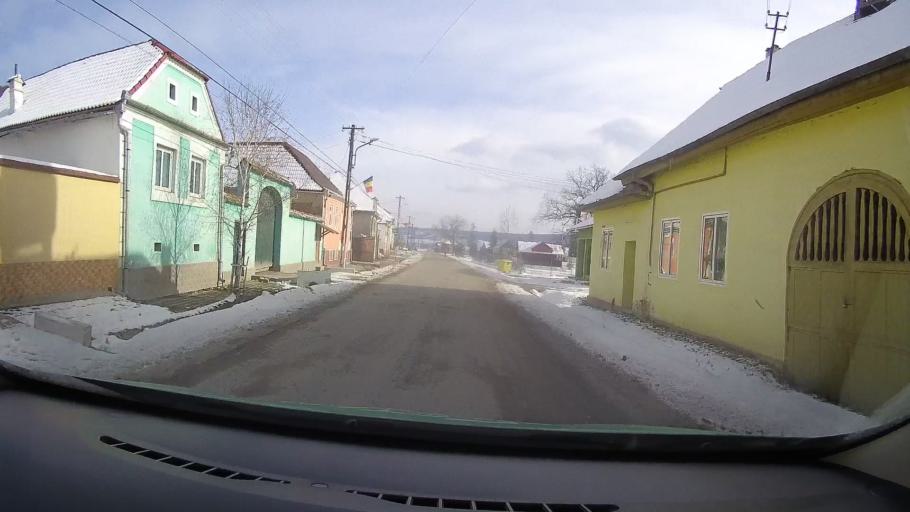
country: RO
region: Sibiu
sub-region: Comuna Iacobeni
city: Iacobeni
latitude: 46.0520
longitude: 24.7154
